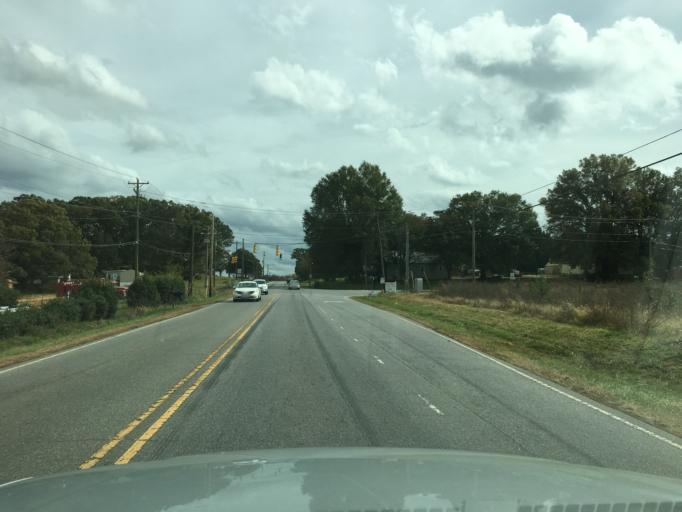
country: US
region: North Carolina
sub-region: Catawba County
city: Hickory
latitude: 35.6940
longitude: -81.2873
